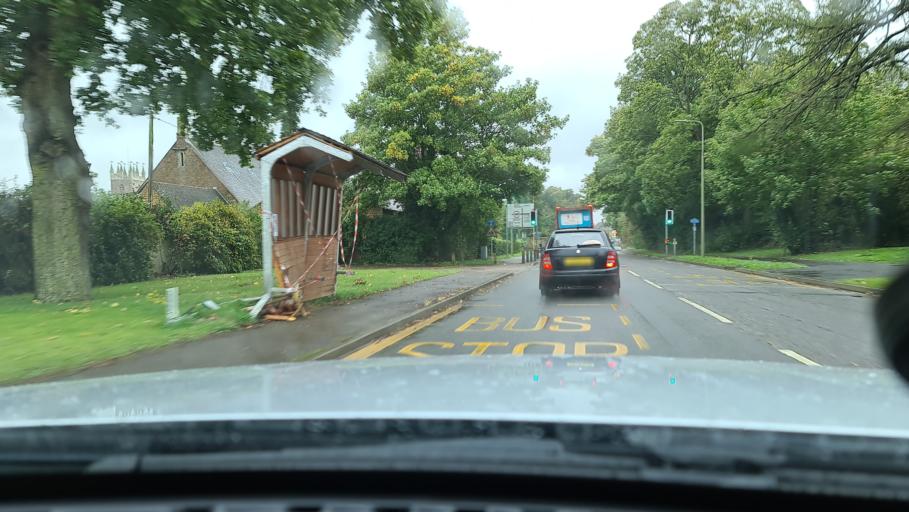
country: GB
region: England
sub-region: Oxfordshire
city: Deddington
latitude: 51.9840
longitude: -1.3227
